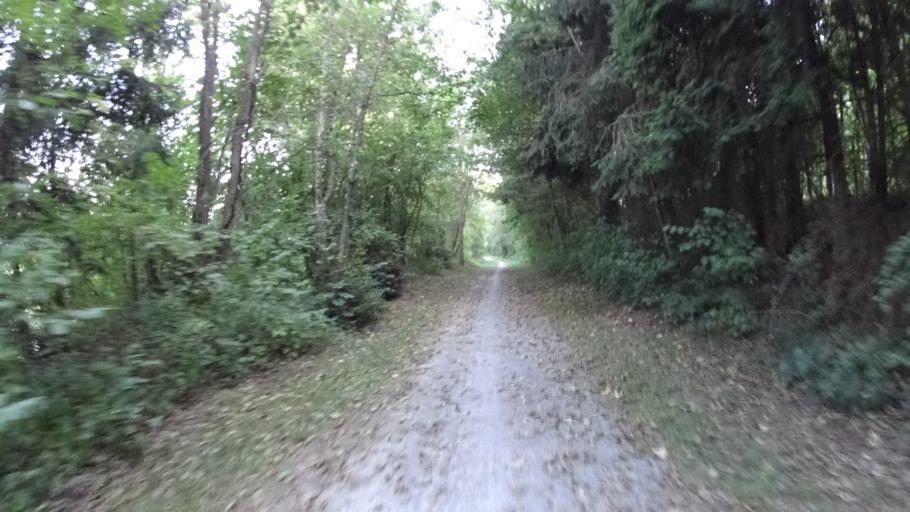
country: AT
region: Carinthia
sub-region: Politischer Bezirk Villach Land
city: Rosegg
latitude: 46.5730
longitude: 14.0218
